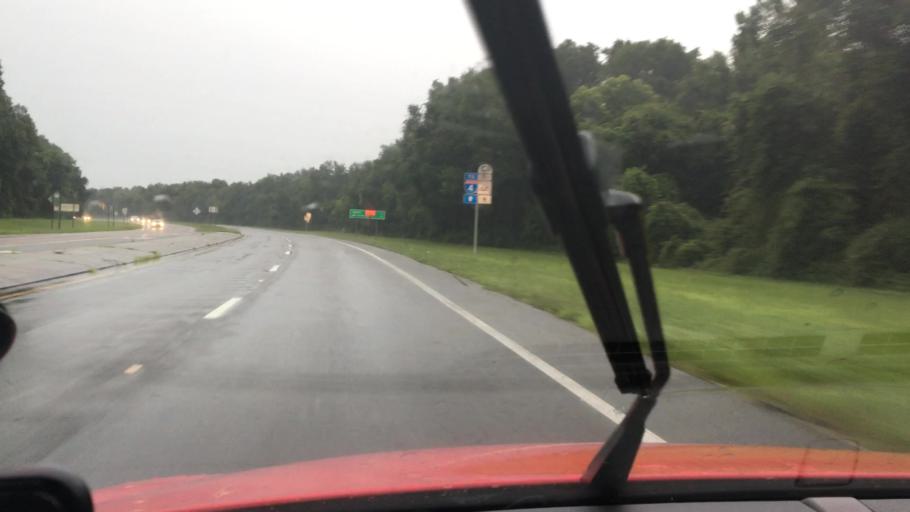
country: US
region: Florida
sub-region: Volusia County
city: Lake Helen
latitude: 29.0153
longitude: -81.2460
